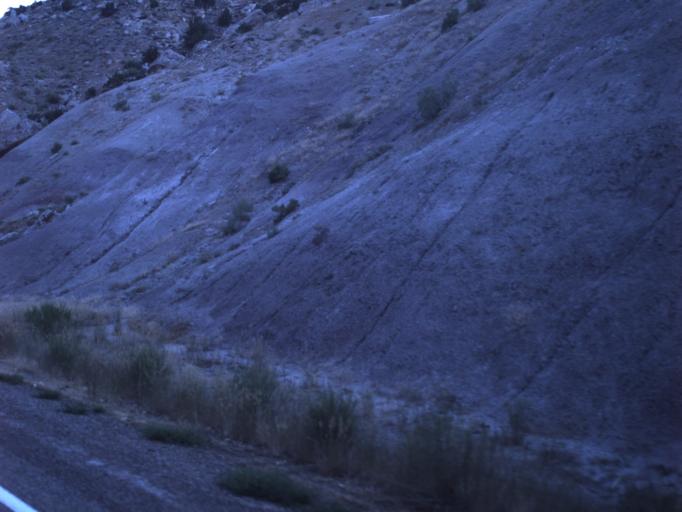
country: US
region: Utah
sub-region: Uintah County
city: Vernal
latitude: 40.5244
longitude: -109.5215
